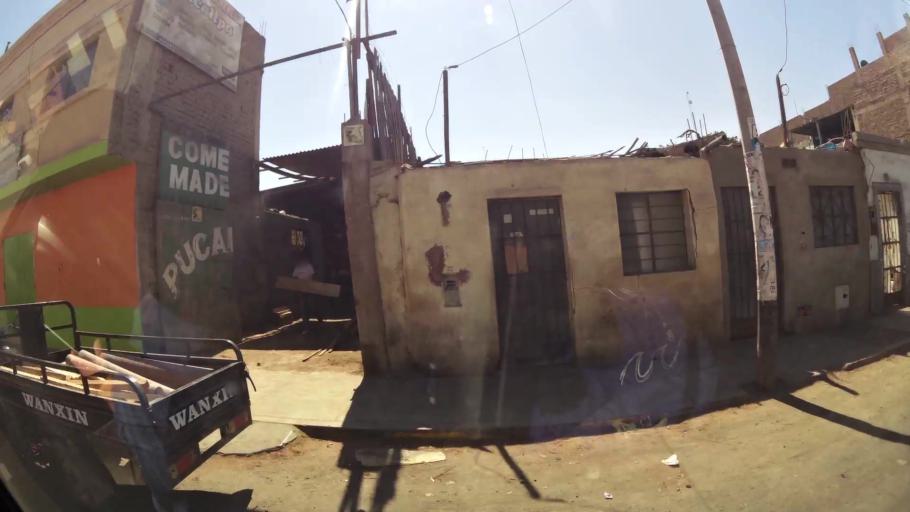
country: PE
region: Ica
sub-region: Provincia de Ica
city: Ica
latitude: -14.0597
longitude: -75.7281
